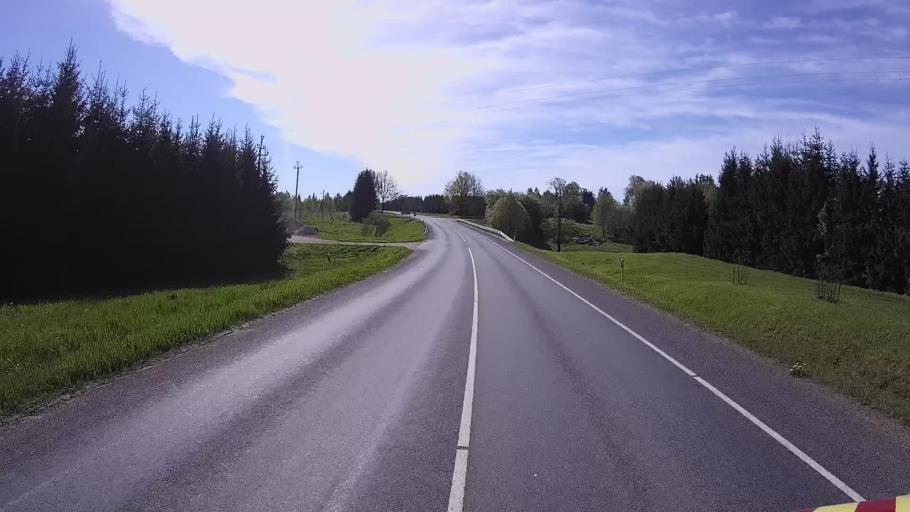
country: EE
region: Polvamaa
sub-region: Polva linn
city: Polva
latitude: 58.1920
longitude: 27.0821
